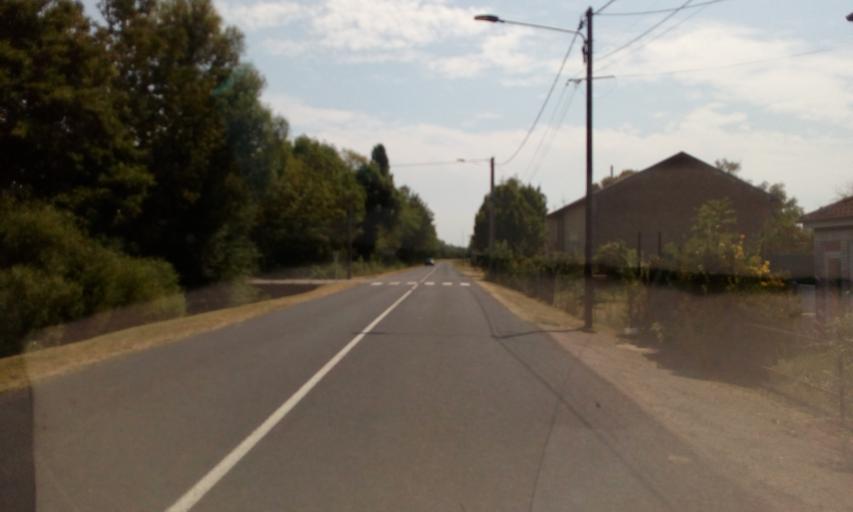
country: FR
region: Lorraine
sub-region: Departement de la Meuse
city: Vigneulles-les-Hattonchatel
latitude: 49.0786
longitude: 5.6399
